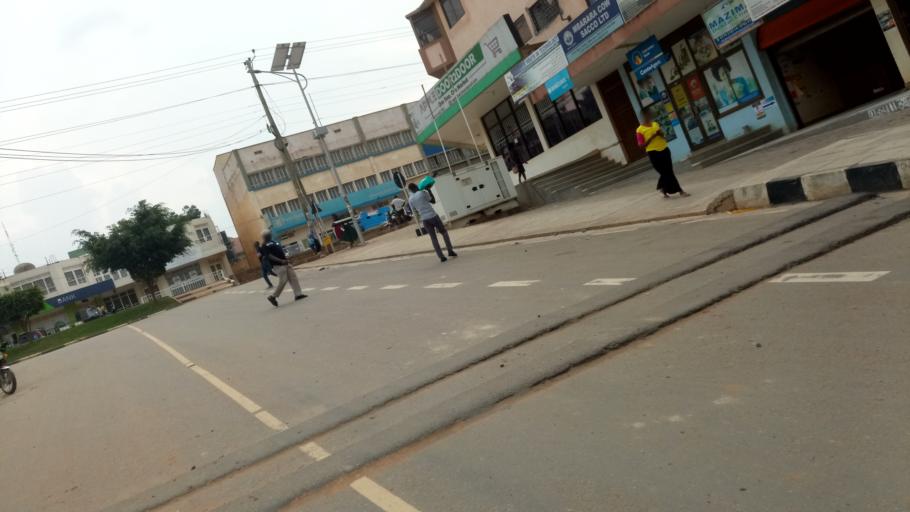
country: UG
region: Western Region
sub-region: Mbarara District
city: Mbarara
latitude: -0.6094
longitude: 30.6611
